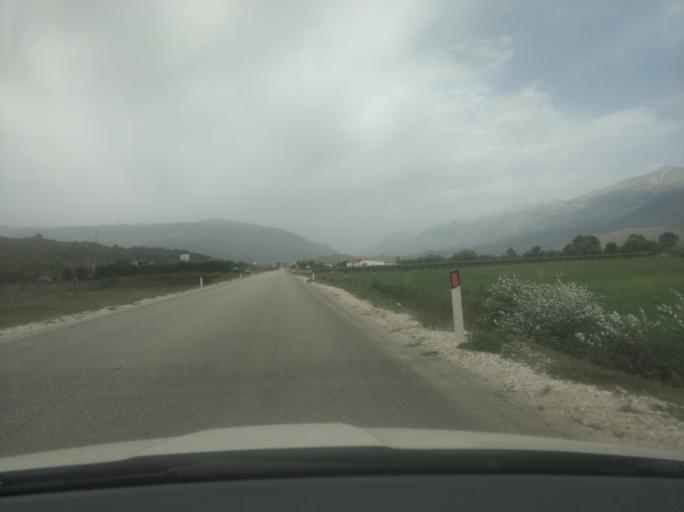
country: AL
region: Gjirokaster
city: Gjirokaster
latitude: 40.1091
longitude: 20.1222
